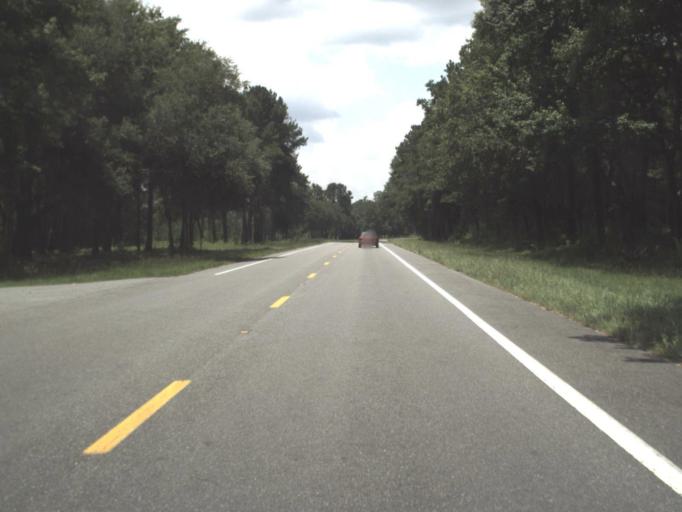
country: US
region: Florida
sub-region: Columbia County
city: Five Points
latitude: 30.2822
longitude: -82.7007
